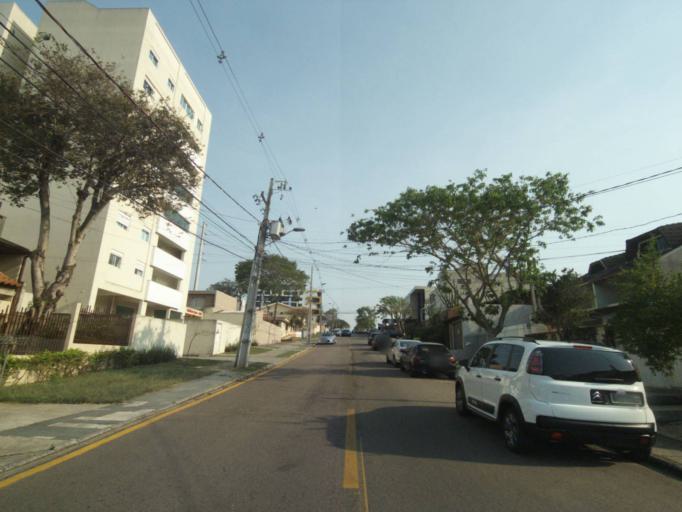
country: BR
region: Parana
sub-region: Curitiba
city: Curitiba
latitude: -25.4621
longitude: -49.2992
